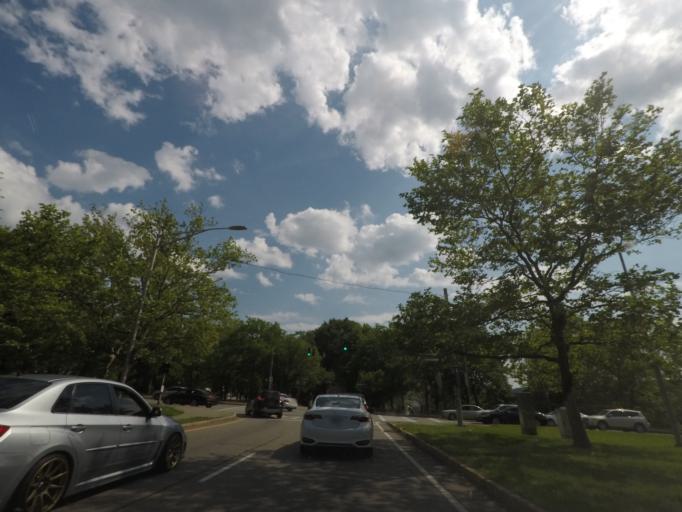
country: US
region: New York
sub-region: Dutchess County
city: Poughkeepsie
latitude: 41.7025
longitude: -73.9309
